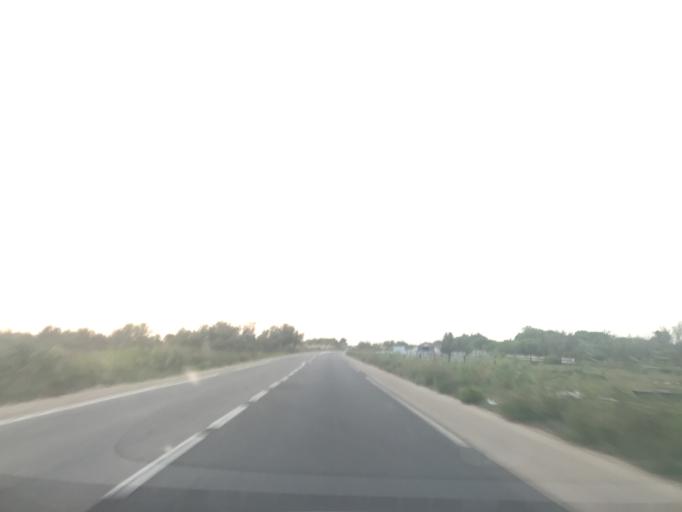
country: FR
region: Provence-Alpes-Cote d'Azur
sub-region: Departement des Bouches-du-Rhone
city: Saintes-Maries-de-la-Mer
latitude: 43.4776
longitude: 4.4080
